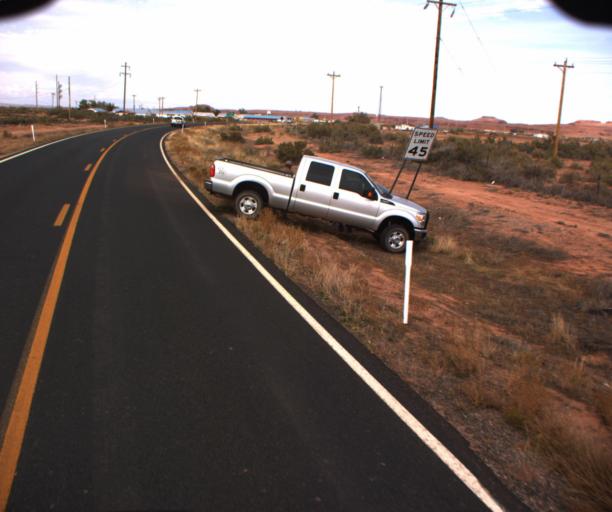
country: US
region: Arizona
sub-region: Apache County
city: Many Farms
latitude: 36.7137
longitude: -109.6253
